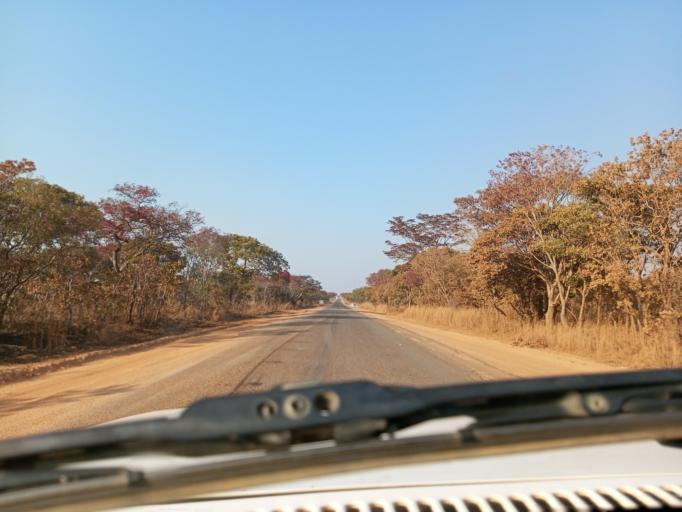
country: ZM
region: Northern
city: Mpika
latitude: -12.3971
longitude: 31.0904
